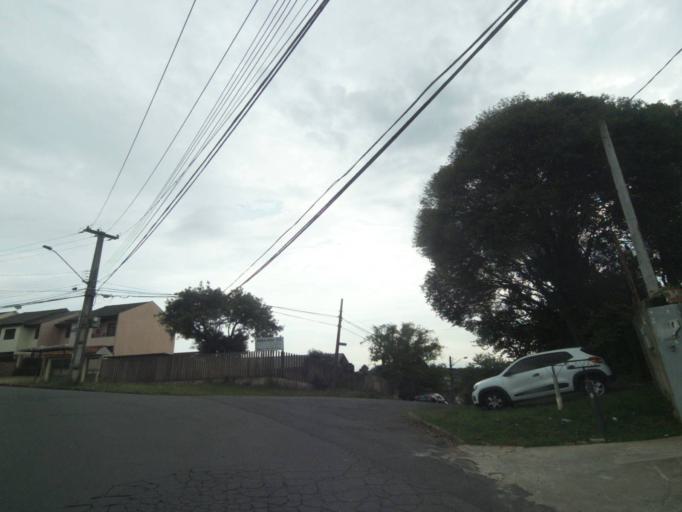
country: BR
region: Parana
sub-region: Curitiba
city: Curitiba
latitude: -25.3938
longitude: -49.2957
